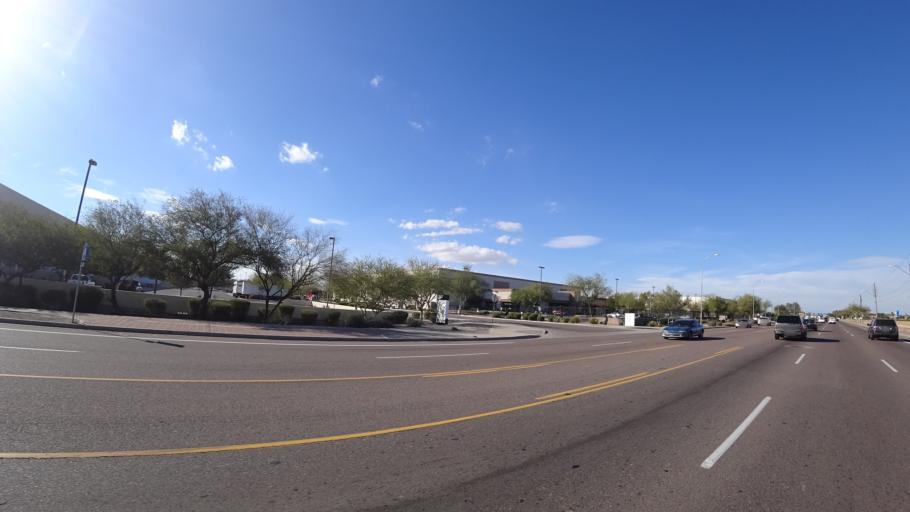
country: US
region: Arizona
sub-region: Maricopa County
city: Tolleson
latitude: 33.4544
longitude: -112.2382
